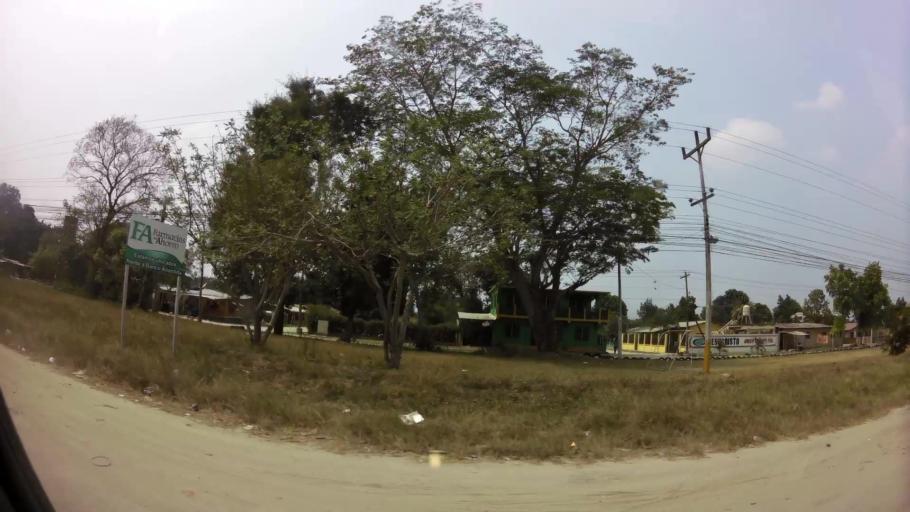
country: HN
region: Cortes
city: La Lima
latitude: 15.4366
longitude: -87.9067
